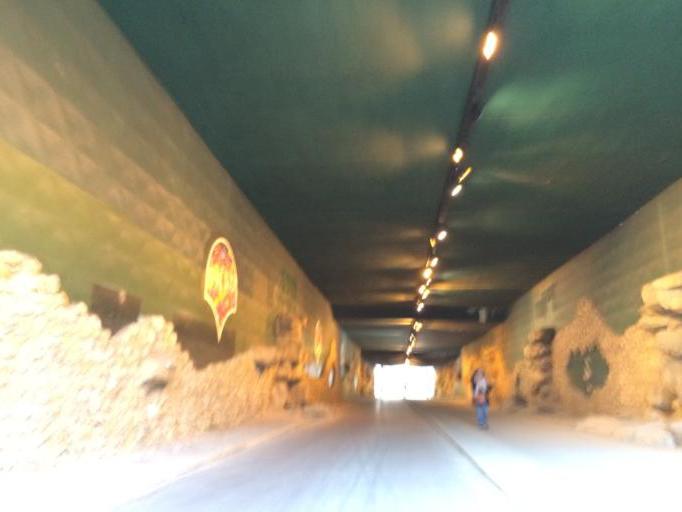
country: FR
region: Ile-de-France
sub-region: Departement du Val-de-Marne
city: Saint-Mande
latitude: 48.8412
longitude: 2.3954
